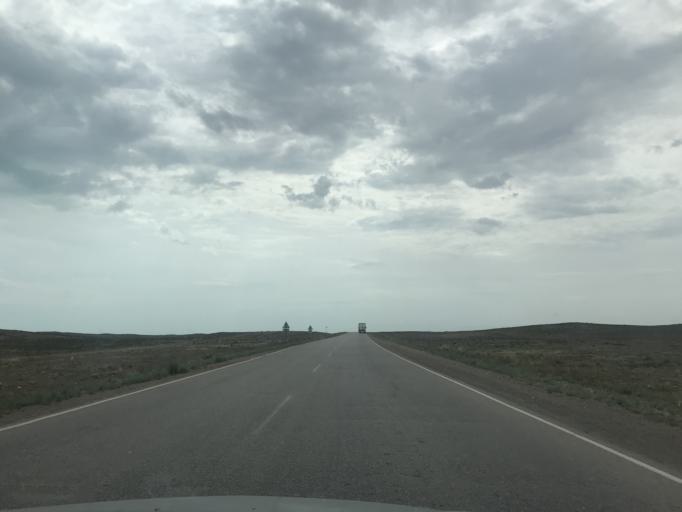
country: KZ
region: Zhambyl
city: Mynaral
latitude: 45.5032
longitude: 73.5106
